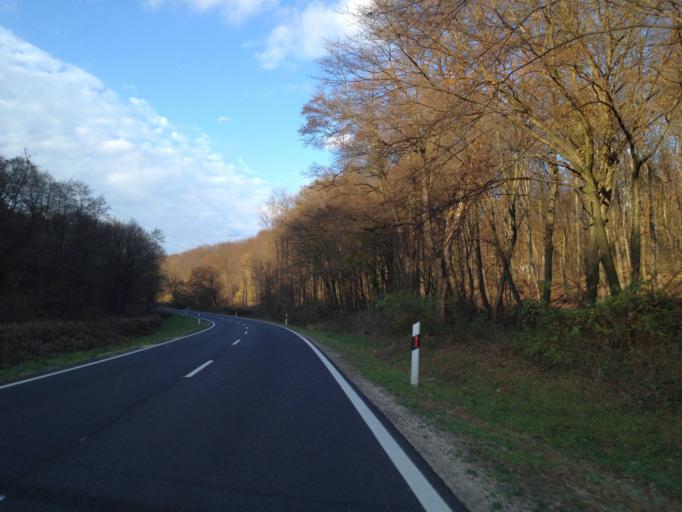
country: HU
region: Gyor-Moson-Sopron
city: Bakonyszentlaszlo
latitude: 47.4040
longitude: 17.8549
